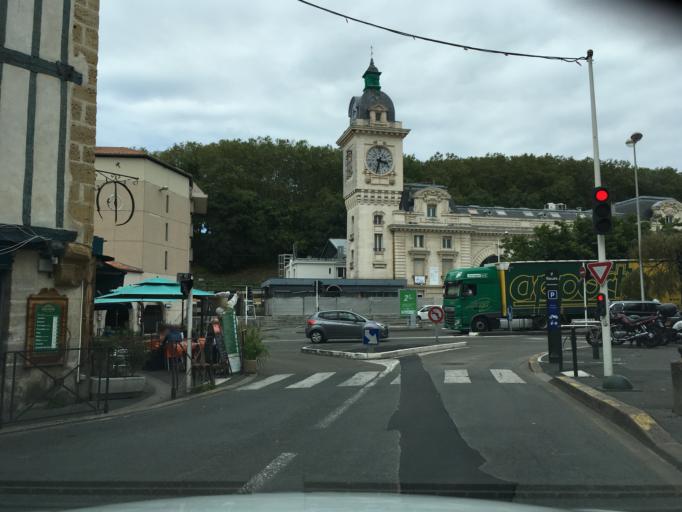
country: FR
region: Aquitaine
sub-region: Departement des Pyrenees-Atlantiques
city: Bayonne
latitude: 43.4960
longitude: -1.4705
